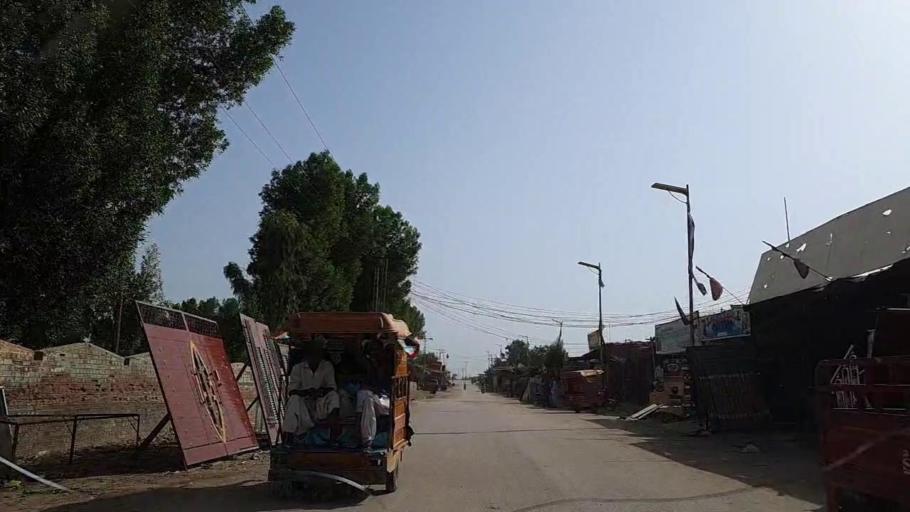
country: PK
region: Sindh
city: Kandiaro
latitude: 27.0552
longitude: 68.2065
